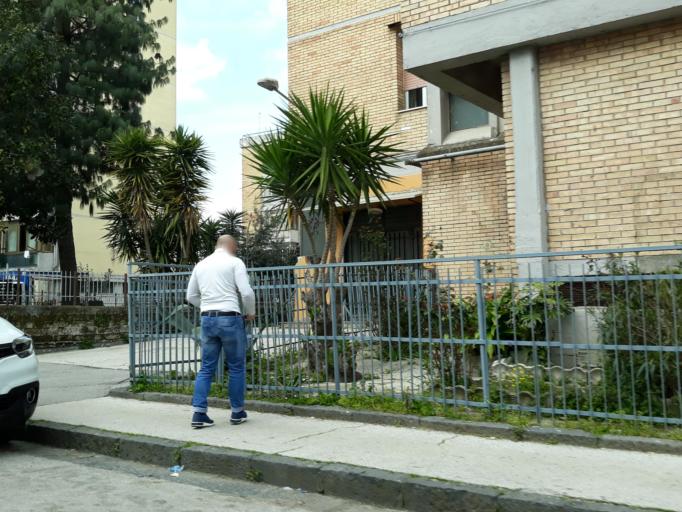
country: IT
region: Campania
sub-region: Provincia di Napoli
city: Melito di Napoli
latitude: 40.8931
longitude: 14.2330
